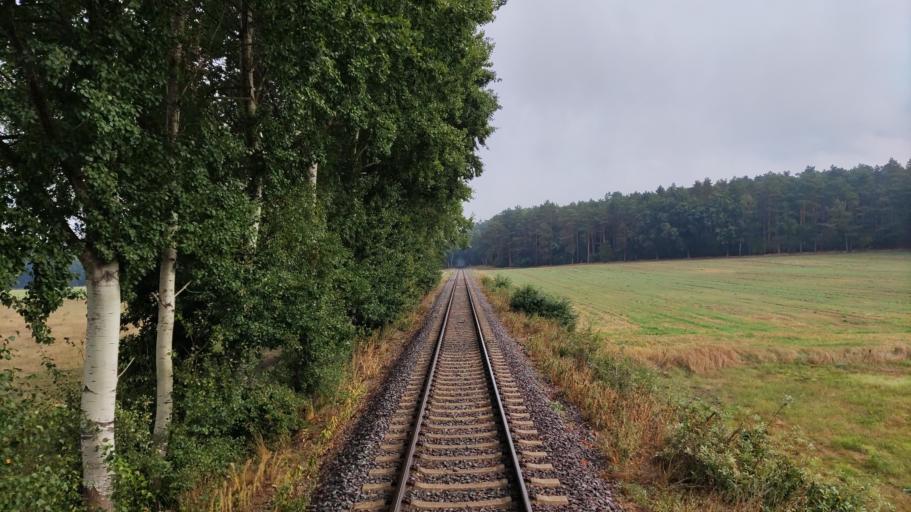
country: DE
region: Lower Saxony
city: Soltau
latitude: 52.9991
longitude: 9.8876
